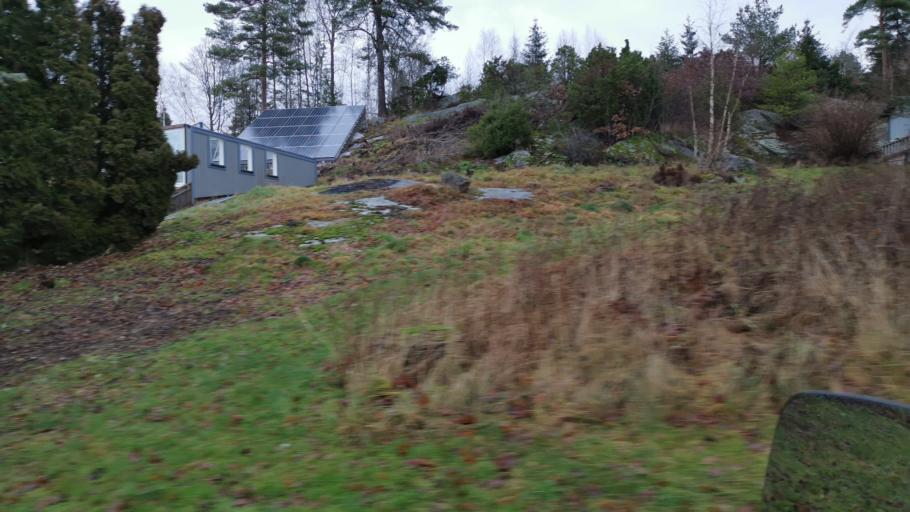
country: SE
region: Vaestra Goetaland
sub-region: Orust
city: Henan
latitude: 58.3464
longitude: 11.6978
